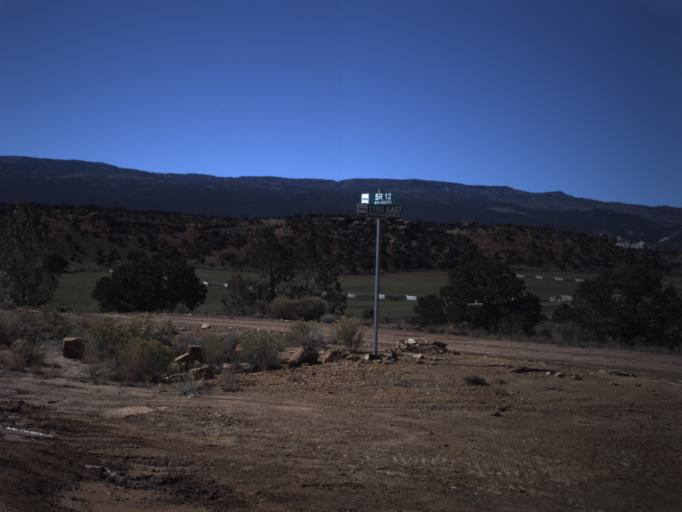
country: US
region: Utah
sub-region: Wayne County
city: Loa
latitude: 38.2852
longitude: -111.3958
